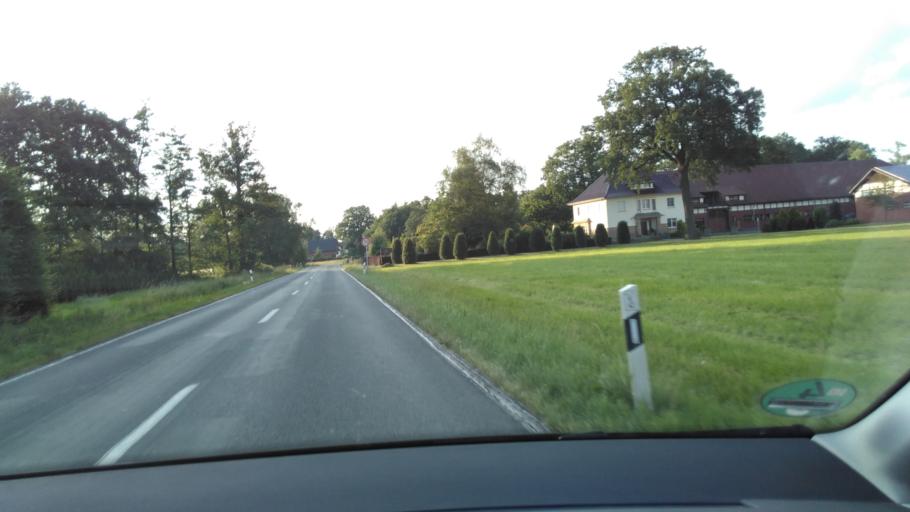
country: DE
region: North Rhine-Westphalia
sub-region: Regierungsbezirk Detmold
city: Verl
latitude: 51.8610
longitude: 8.5001
